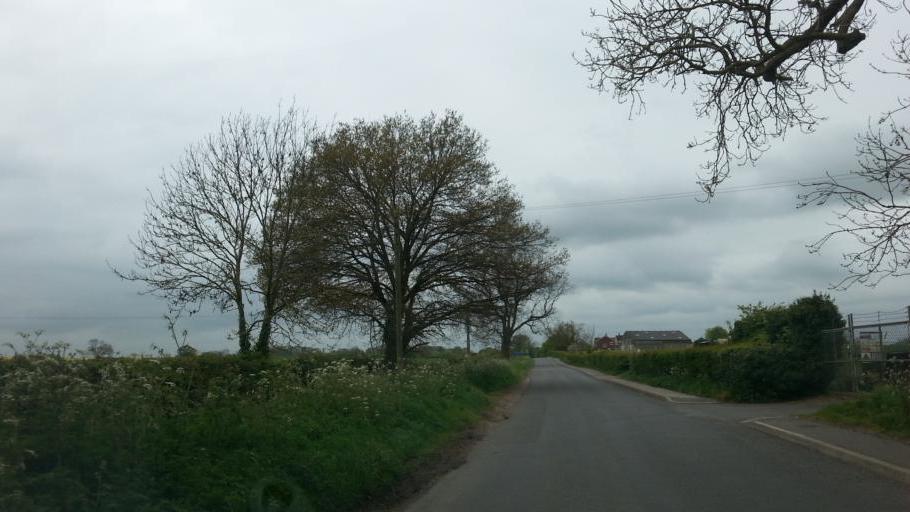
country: GB
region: England
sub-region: Lincolnshire
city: Bourne
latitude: 52.8593
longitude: -0.4844
